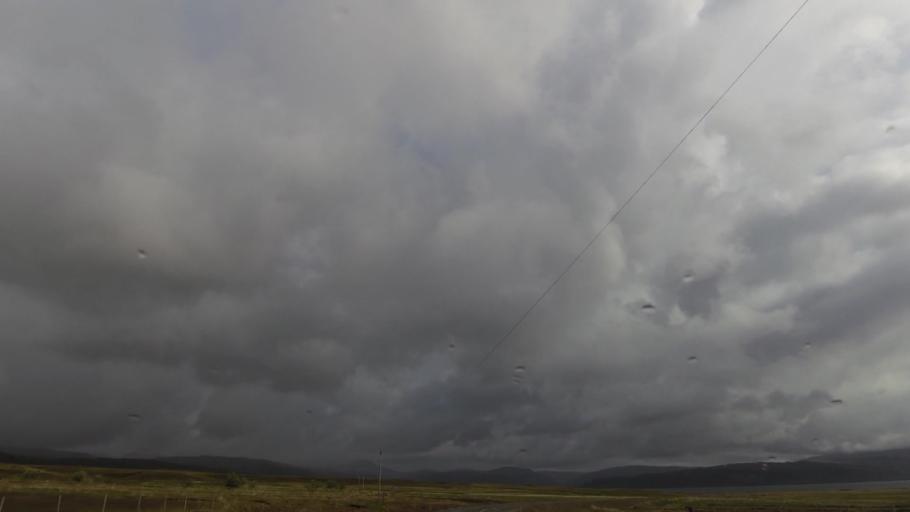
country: IS
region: Westfjords
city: Isafjoerdur
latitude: 65.5100
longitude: -23.1935
